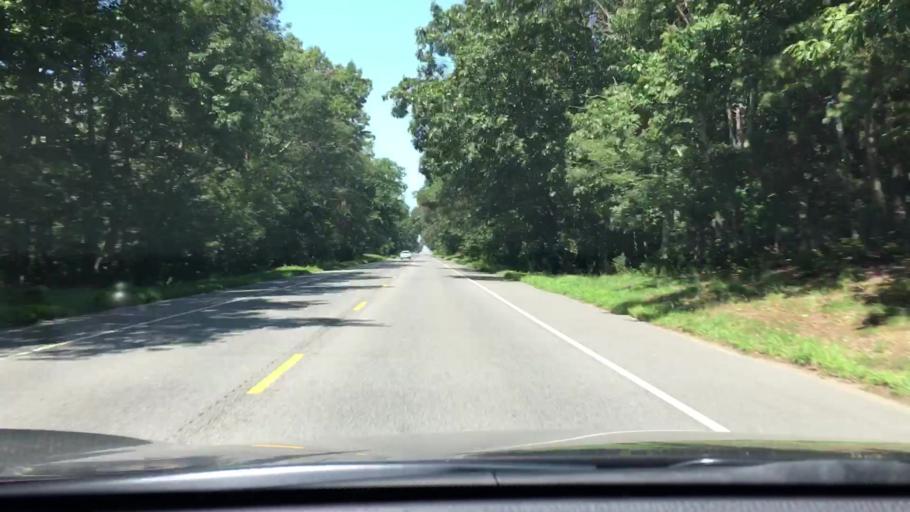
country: US
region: New Jersey
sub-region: Cumberland County
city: Laurel Lake
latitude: 39.3492
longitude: -75.0508
